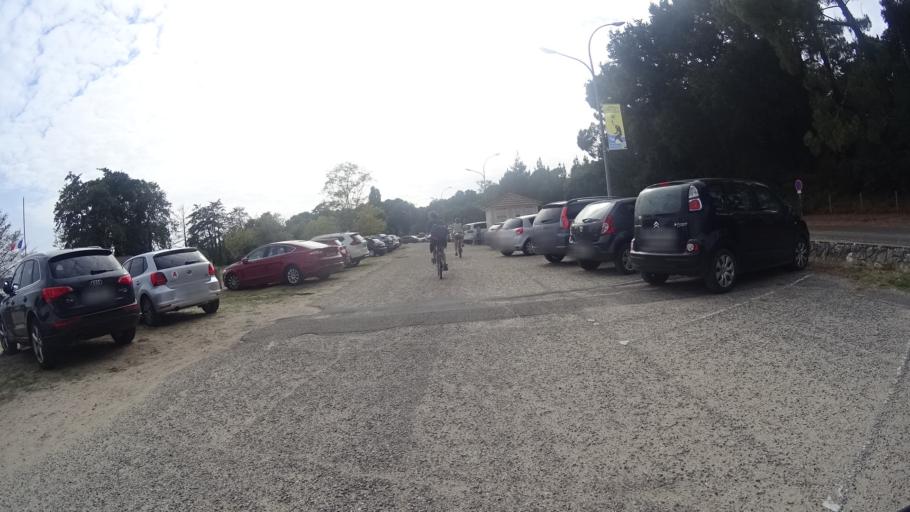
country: FR
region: Aquitaine
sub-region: Departement de la Gironde
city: Lacanau
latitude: 45.0023
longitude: -1.1356
